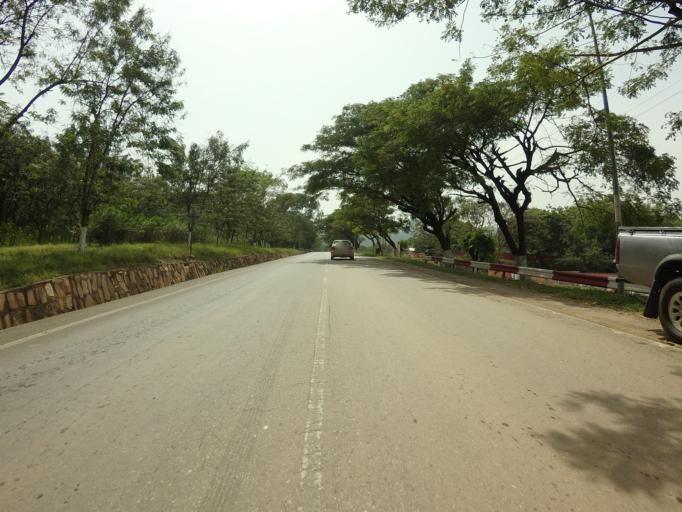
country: GH
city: Akropong
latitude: 6.2749
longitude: 0.0531
